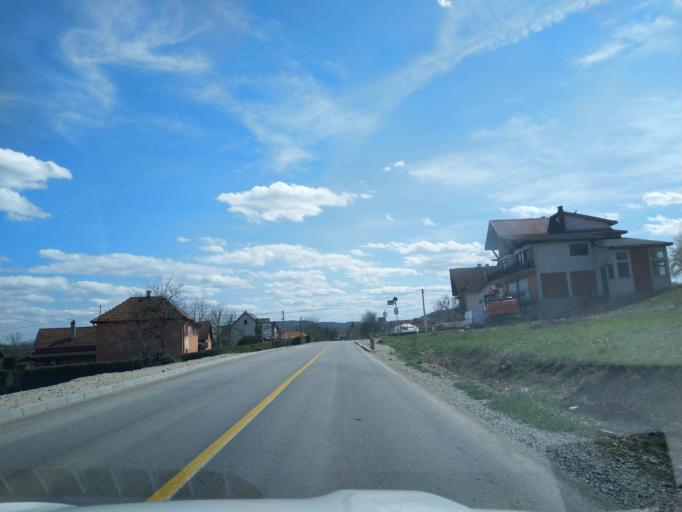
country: RS
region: Central Serbia
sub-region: Zlatiborski Okrug
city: Pozega
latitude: 43.8148
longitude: 20.0881
